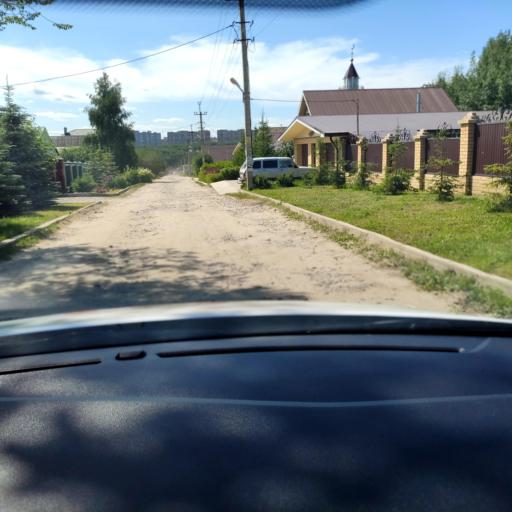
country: RU
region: Tatarstan
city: Stolbishchi
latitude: 55.7773
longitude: 49.2625
